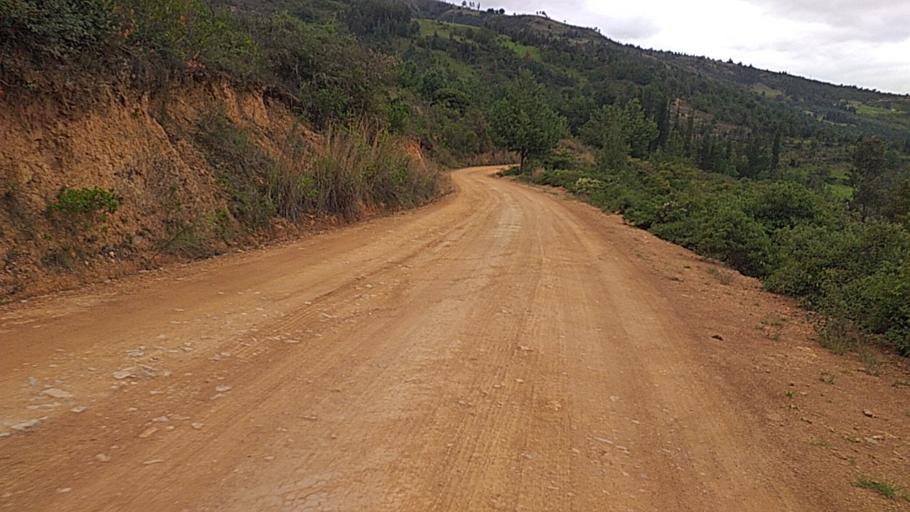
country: CO
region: Boyaca
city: Floresta
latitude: 5.8789
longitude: -72.9129
